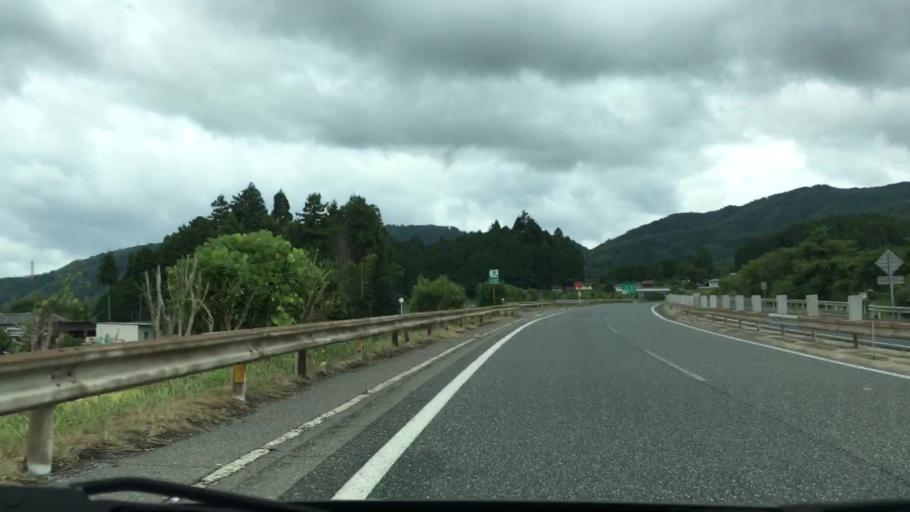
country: JP
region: Okayama
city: Takahashi
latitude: 34.9772
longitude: 133.6697
